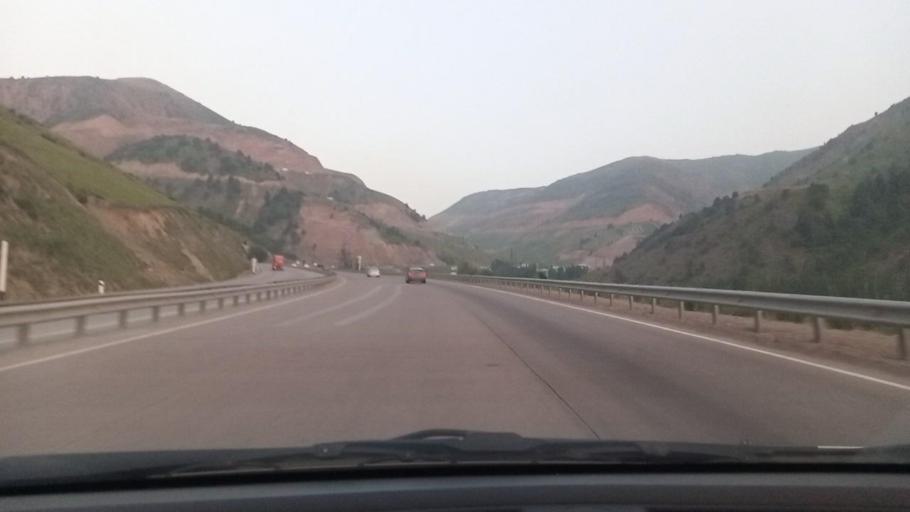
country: UZ
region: Toshkent
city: Angren
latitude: 41.1193
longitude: 70.4899
